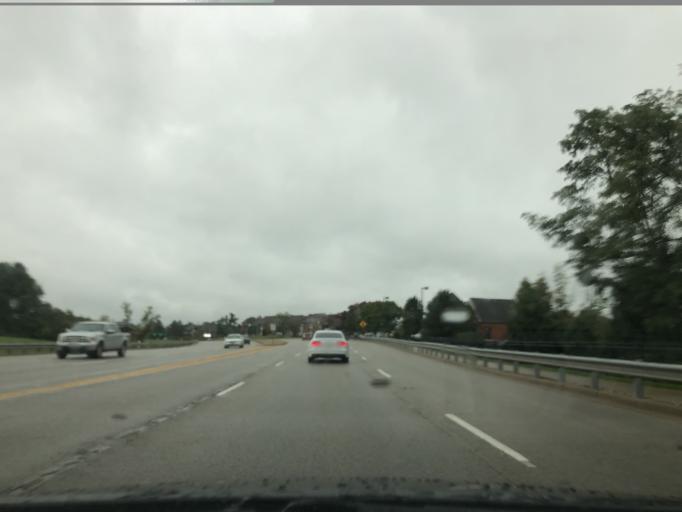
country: US
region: Ohio
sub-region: Hamilton County
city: Highpoint
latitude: 39.2677
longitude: -84.3776
